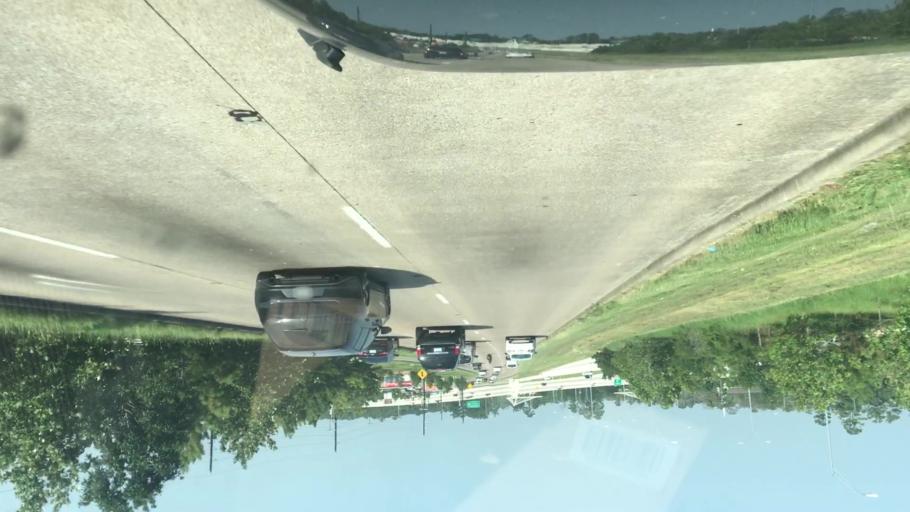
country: US
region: Texas
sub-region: Harris County
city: Atascocita
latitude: 29.9303
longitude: -95.2050
